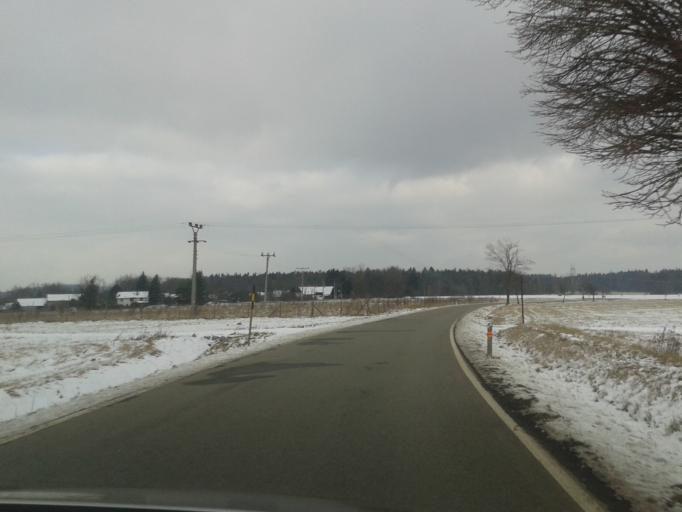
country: CZ
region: Olomoucky
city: Horni Stepanov
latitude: 49.5839
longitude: 16.8300
